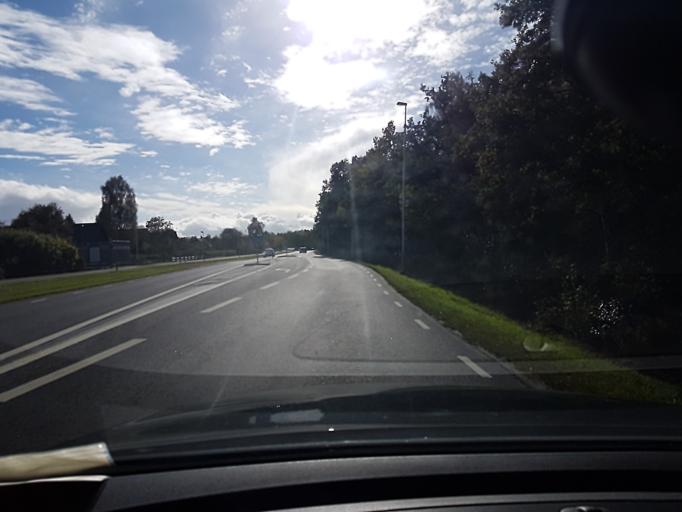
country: SE
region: Kronoberg
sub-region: Vaxjo Kommun
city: Vaexjoe
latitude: 56.8581
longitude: 14.8091
